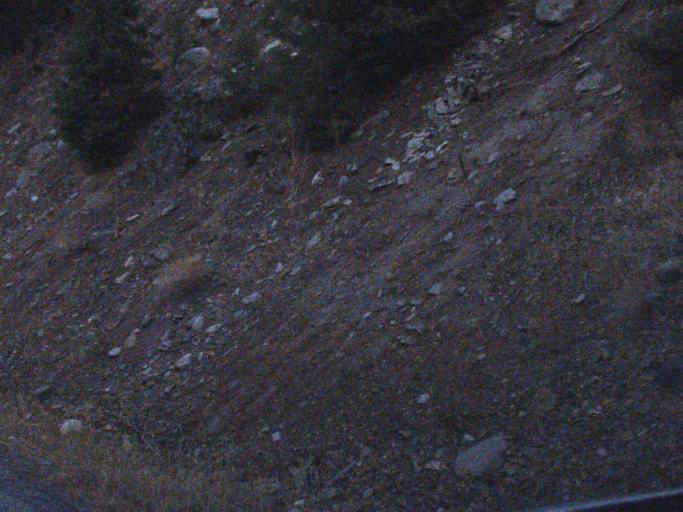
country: US
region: Washington
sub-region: Ferry County
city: Republic
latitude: 48.5506
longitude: -118.7474
